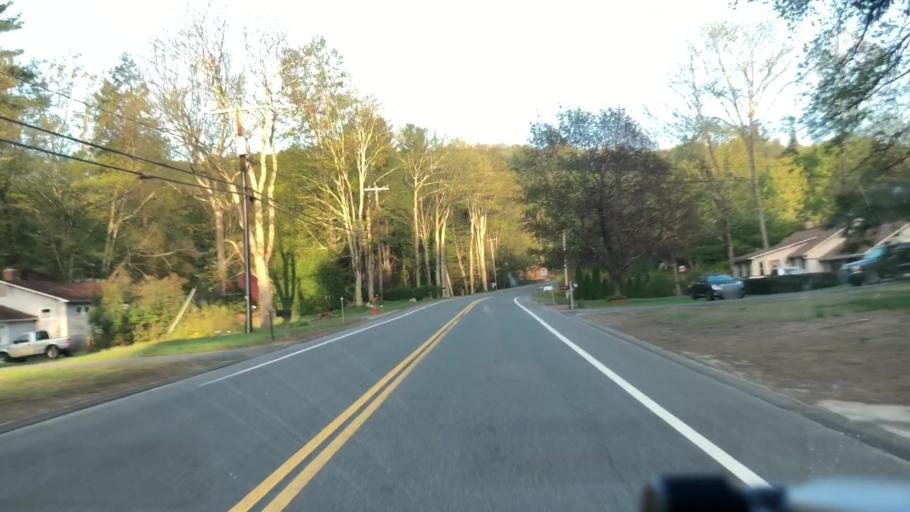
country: US
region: Massachusetts
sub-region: Hampshire County
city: Westhampton
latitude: 42.2819
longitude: -72.7882
